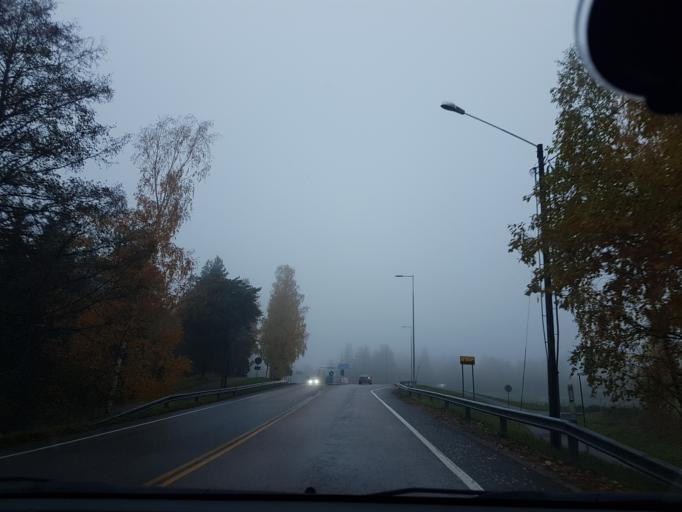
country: FI
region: Uusimaa
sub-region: Helsinki
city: Jaervenpaeae
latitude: 60.4531
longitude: 25.0818
